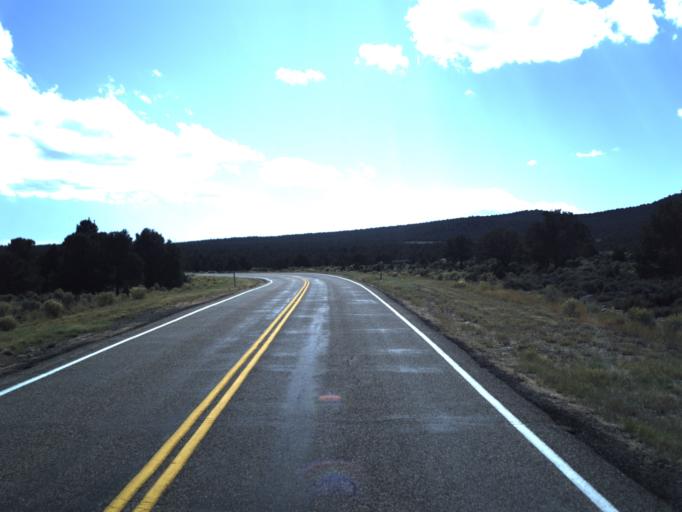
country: US
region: Utah
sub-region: Garfield County
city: Panguitch
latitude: 37.7908
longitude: -112.4381
